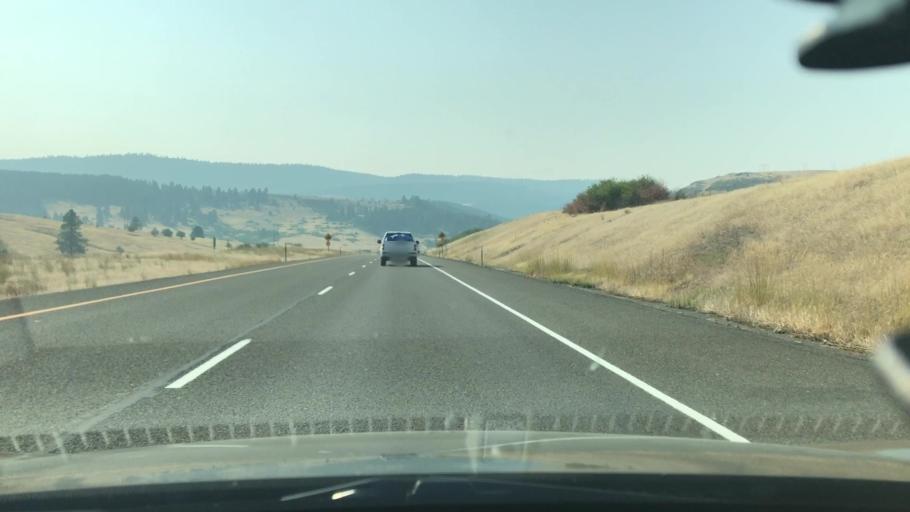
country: US
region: Oregon
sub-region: Union County
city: Union
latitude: 45.1910
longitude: -117.9999
